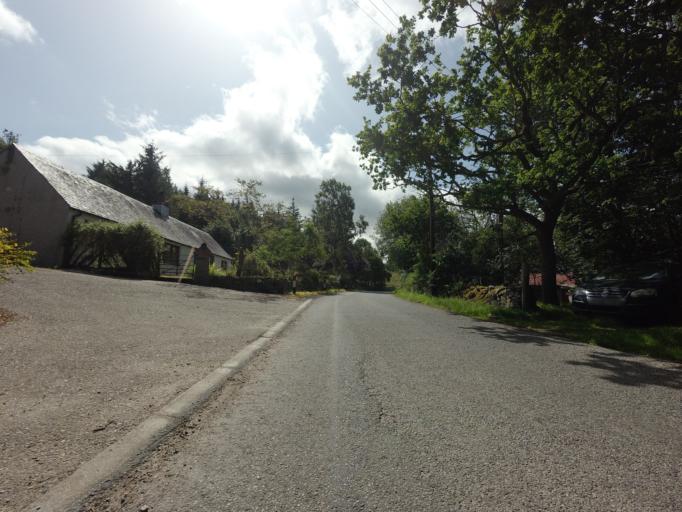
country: GB
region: Scotland
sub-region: Highland
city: Nairn
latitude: 57.4973
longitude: -3.9991
